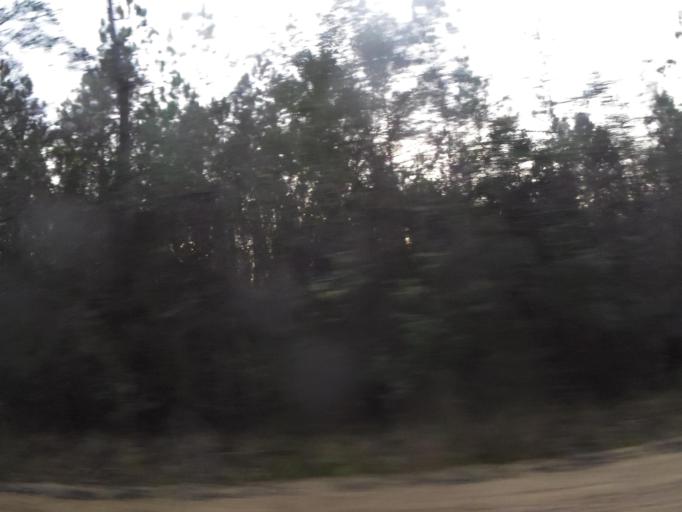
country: US
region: Florida
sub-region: Clay County
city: Asbury Lake
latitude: 29.9509
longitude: -81.7886
